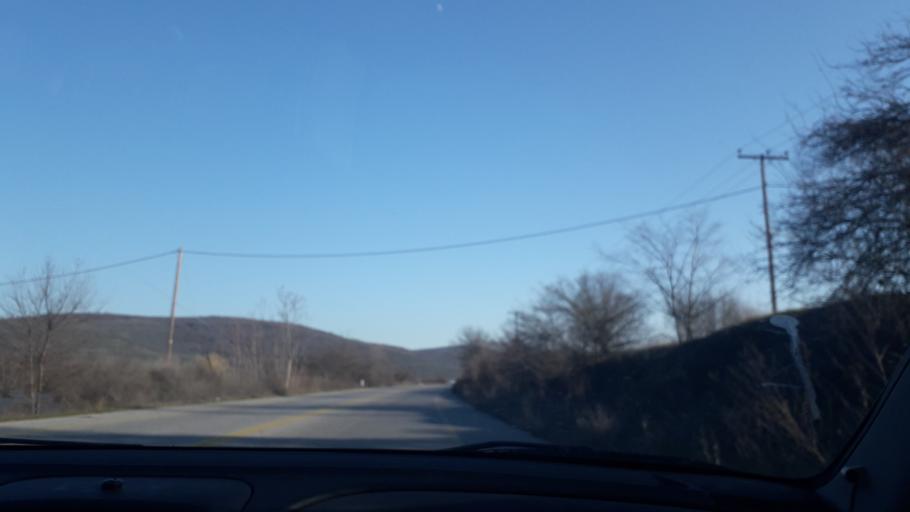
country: GR
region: Central Macedonia
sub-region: Nomos Pellis
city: Apsalos
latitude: 40.8858
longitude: 22.0751
